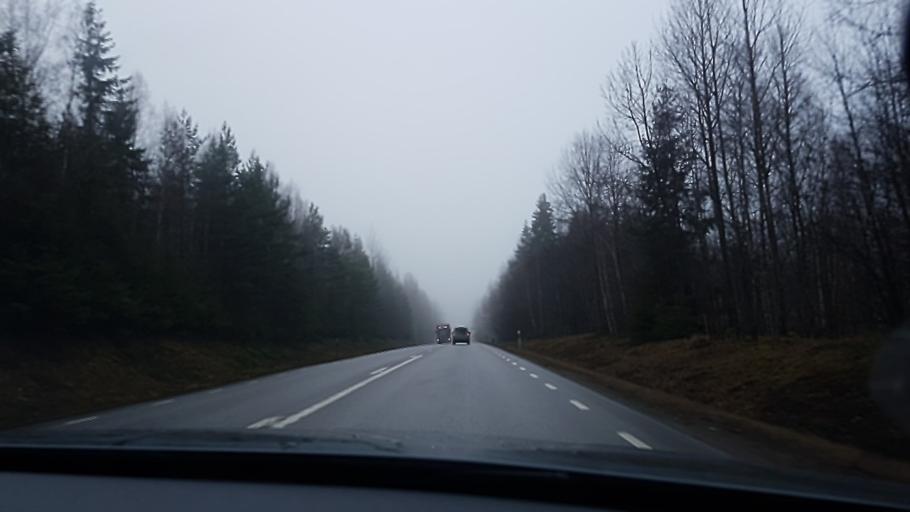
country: SE
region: Vaestra Goetaland
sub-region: Gullspangs Kommun
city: Gullspang
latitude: 58.9729
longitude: 14.0752
